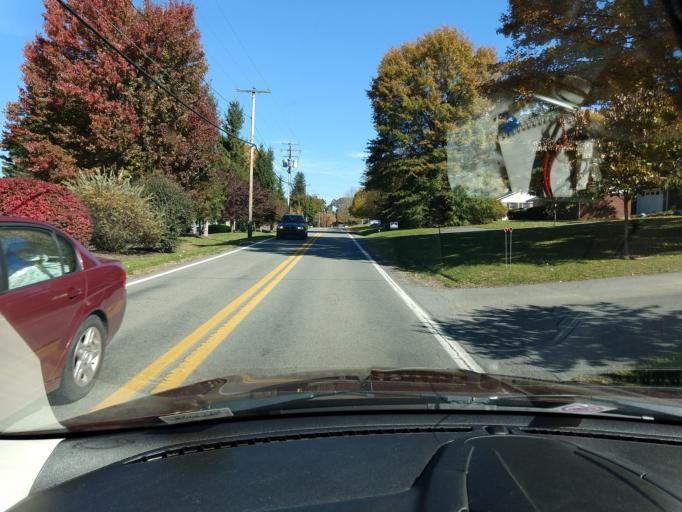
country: US
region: West Virginia
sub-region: Greenbrier County
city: Lewisburg
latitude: 37.7930
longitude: -80.4448
